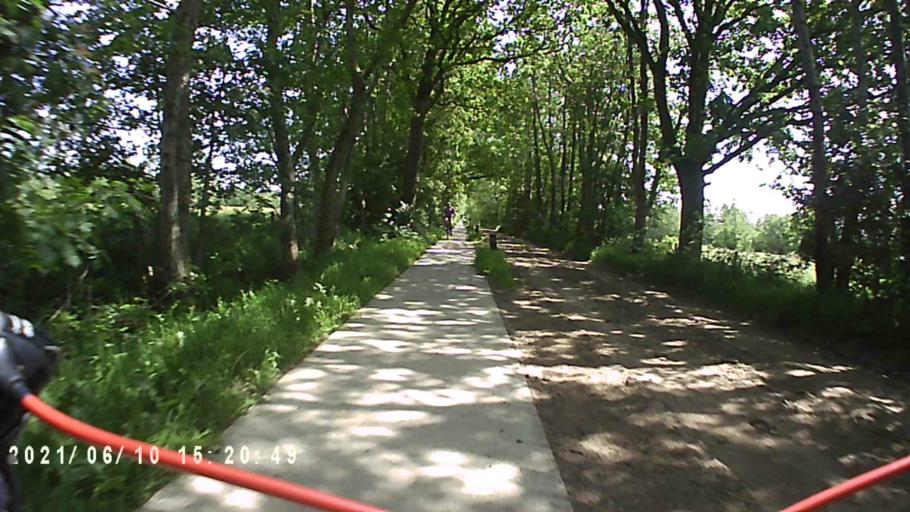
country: NL
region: Friesland
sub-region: Gemeente Achtkarspelen
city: Surhuisterveen
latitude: 53.1914
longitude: 6.1785
